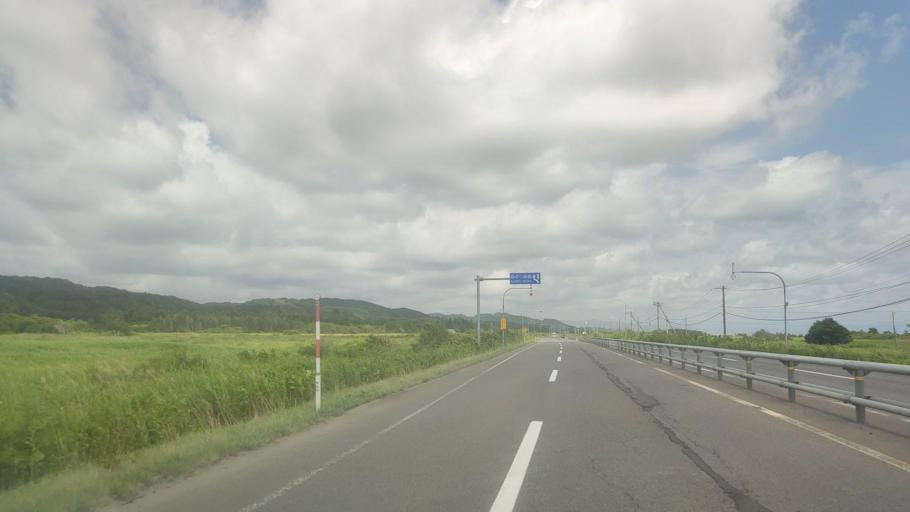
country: JP
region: Hokkaido
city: Niseko Town
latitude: 42.4067
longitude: 140.3055
